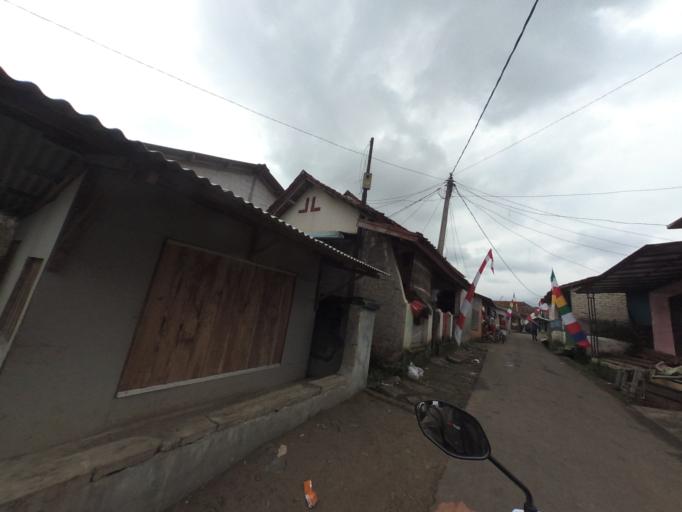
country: ID
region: West Java
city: Bogor
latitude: -6.6105
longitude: 106.7381
